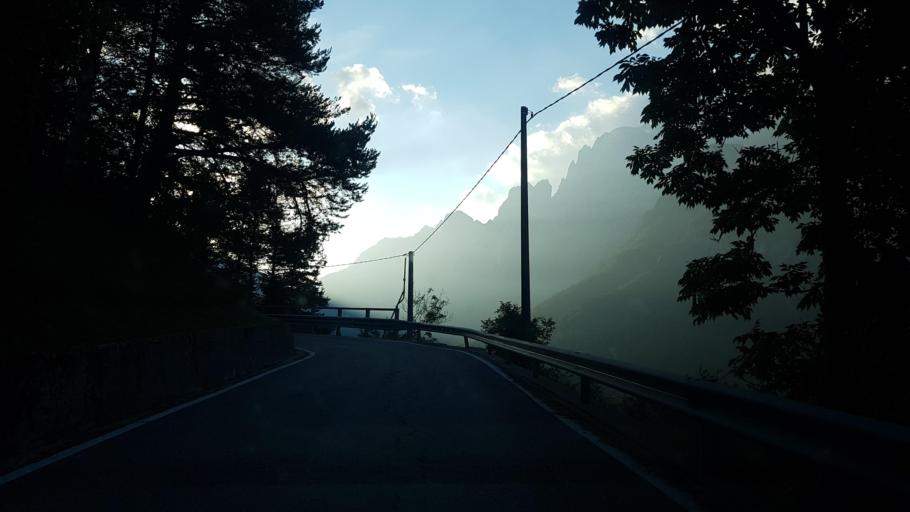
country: IT
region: Friuli Venezia Giulia
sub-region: Provincia di Udine
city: Dogna
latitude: 46.4507
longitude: 13.3697
